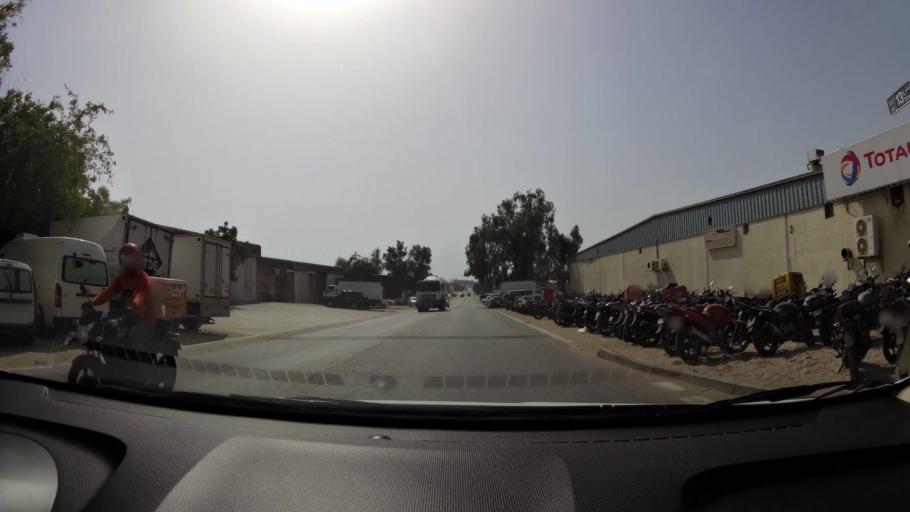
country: AE
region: Ash Shariqah
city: Sharjah
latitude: 25.2301
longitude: 55.3727
